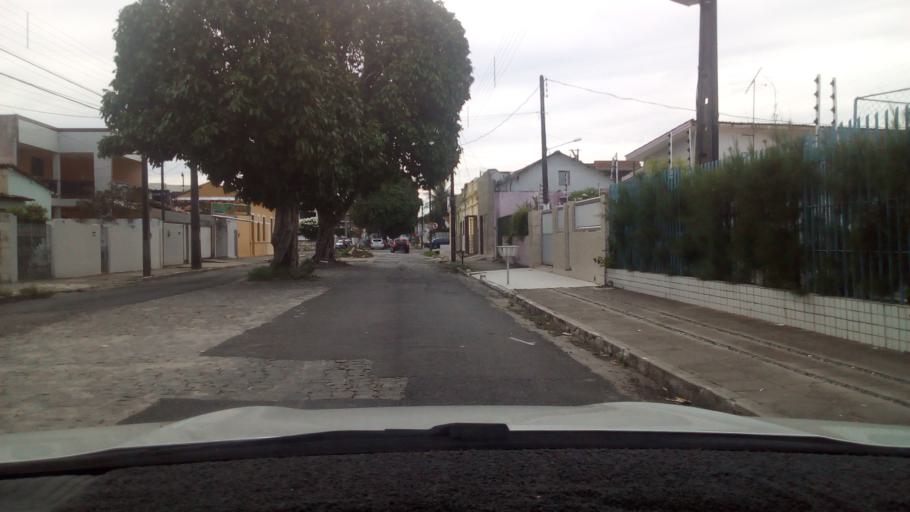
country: BR
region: Paraiba
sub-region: Joao Pessoa
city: Joao Pessoa
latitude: -7.1351
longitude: -34.8767
